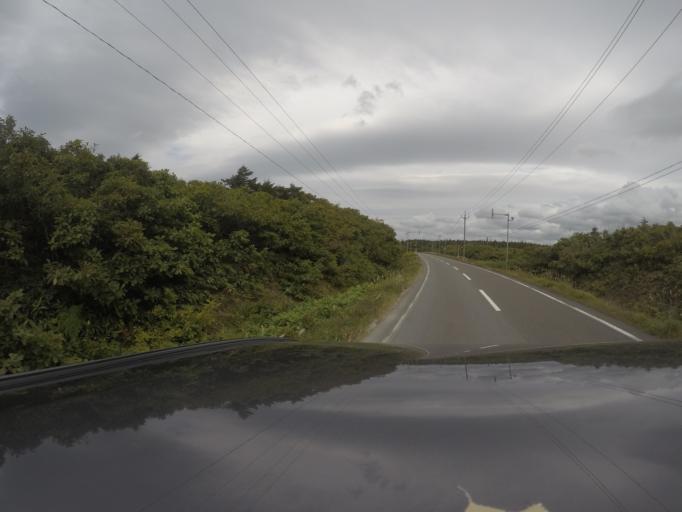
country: JP
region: Hokkaido
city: Makubetsu
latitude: 44.9964
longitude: 141.6936
